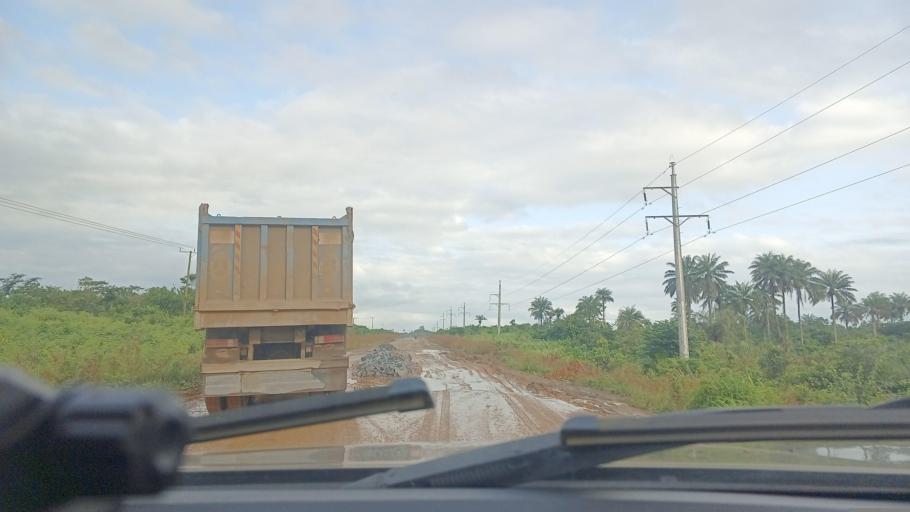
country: LR
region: Montserrado
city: Monrovia
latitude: 6.5746
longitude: -10.8830
